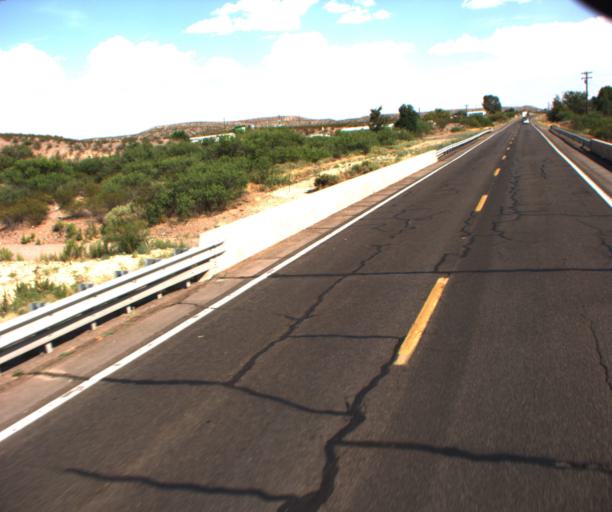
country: US
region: Arizona
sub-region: Greenlee County
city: Clifton
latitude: 32.8258
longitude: -109.1748
